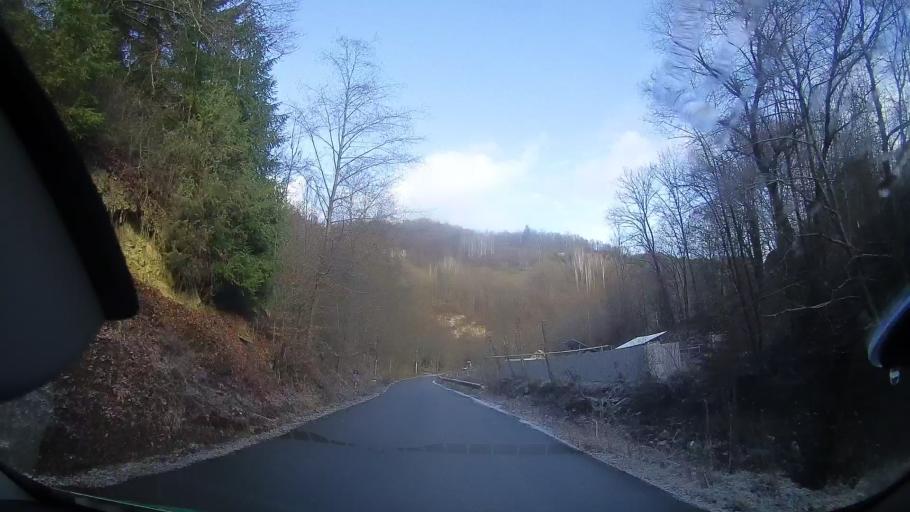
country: RO
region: Alba
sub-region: Comuna Sohodol
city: Sohodol
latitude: 46.3477
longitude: 23.0203
